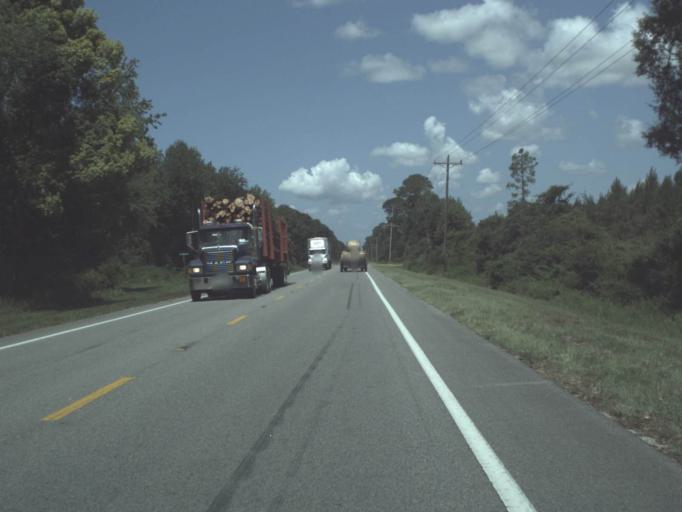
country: US
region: Florida
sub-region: Taylor County
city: Perry
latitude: 30.0933
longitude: -83.6832
